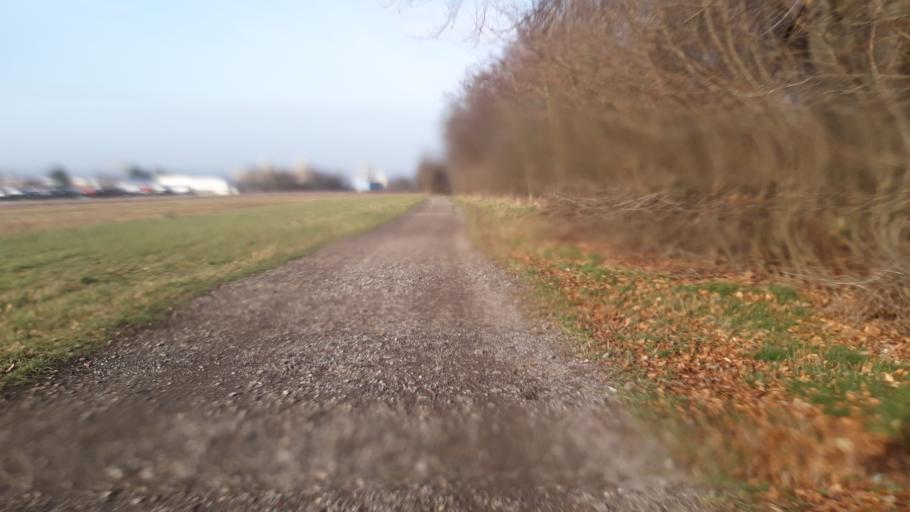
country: DE
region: North Rhine-Westphalia
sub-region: Regierungsbezirk Detmold
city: Paderborn
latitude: 51.6876
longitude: 8.7527
